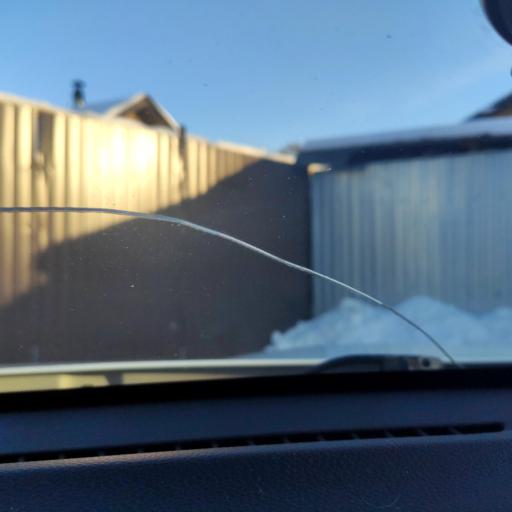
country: RU
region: Tatarstan
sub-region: Gorod Kazan'
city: Kazan
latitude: 55.7284
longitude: 49.1381
